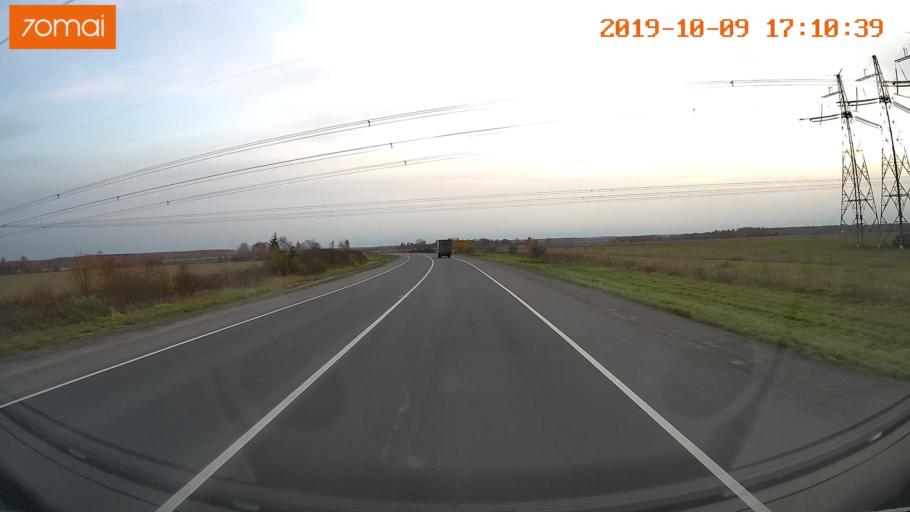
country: RU
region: Ivanovo
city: Privolzhsk
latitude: 57.3531
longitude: 41.2565
